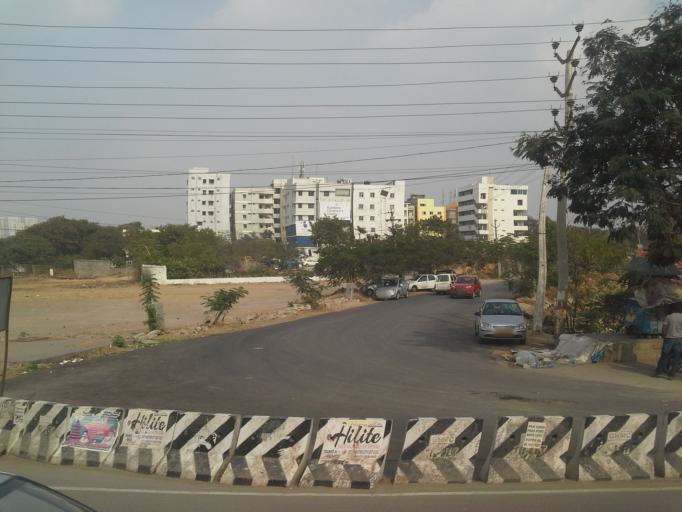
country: IN
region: Telangana
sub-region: Rangareddi
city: Kukatpalli
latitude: 17.4540
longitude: 78.3791
